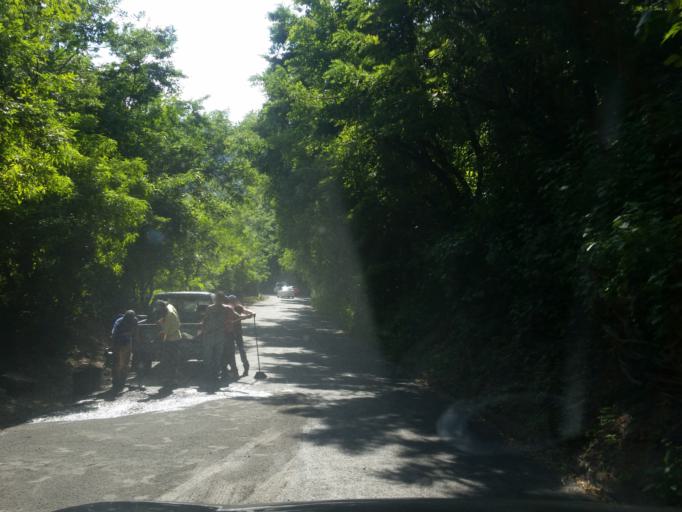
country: NI
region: Masaya
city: Catarina
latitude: 11.9438
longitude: -86.0509
